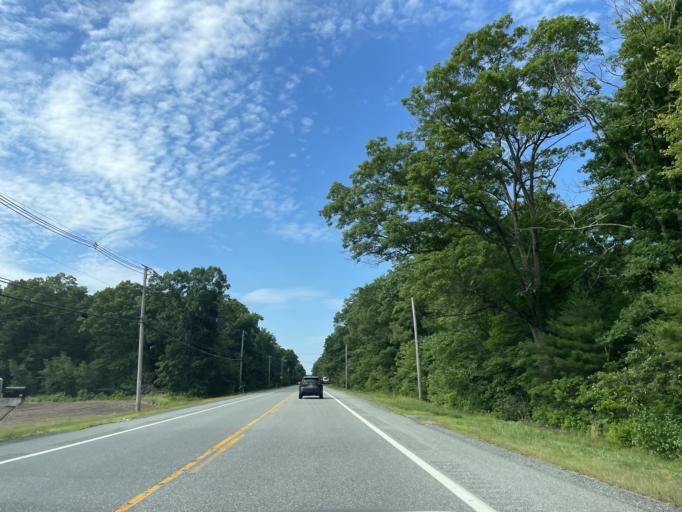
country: US
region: Rhode Island
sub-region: Kent County
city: West Greenwich
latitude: 41.6597
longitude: -71.6949
